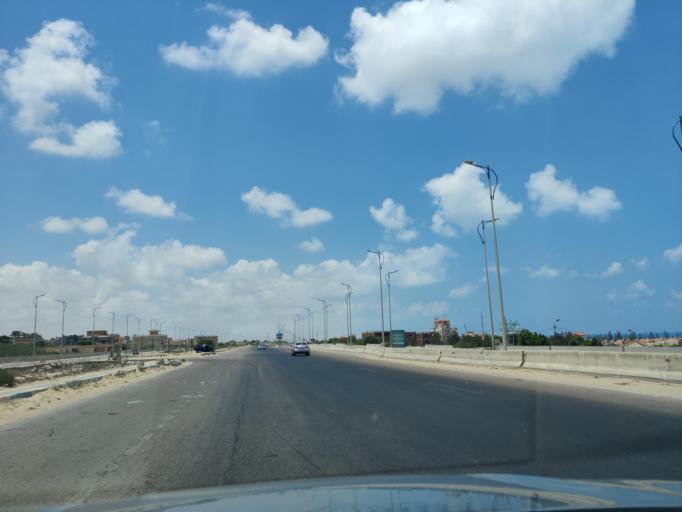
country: EG
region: Alexandria
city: Alexandria
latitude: 30.9646
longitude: 29.5508
